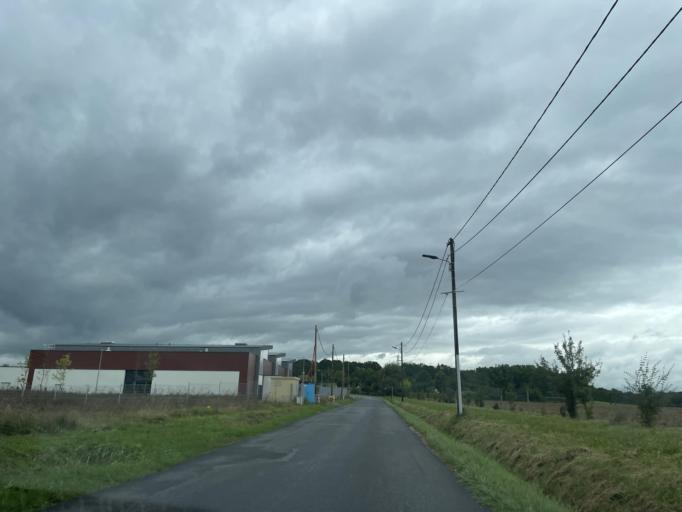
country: FR
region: Ile-de-France
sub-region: Departement de Seine-et-Marne
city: Coulommiers
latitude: 48.8137
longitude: 3.1097
